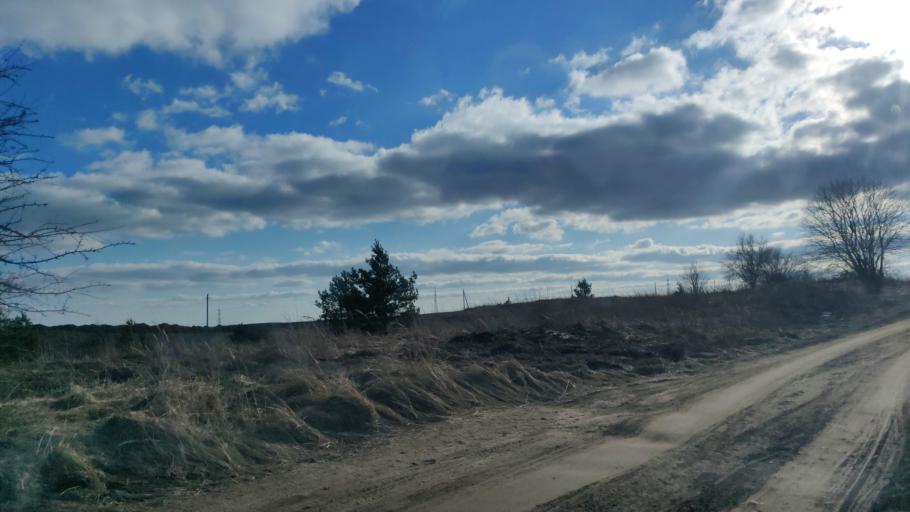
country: LT
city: Lentvaris
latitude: 54.6110
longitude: 24.9999
